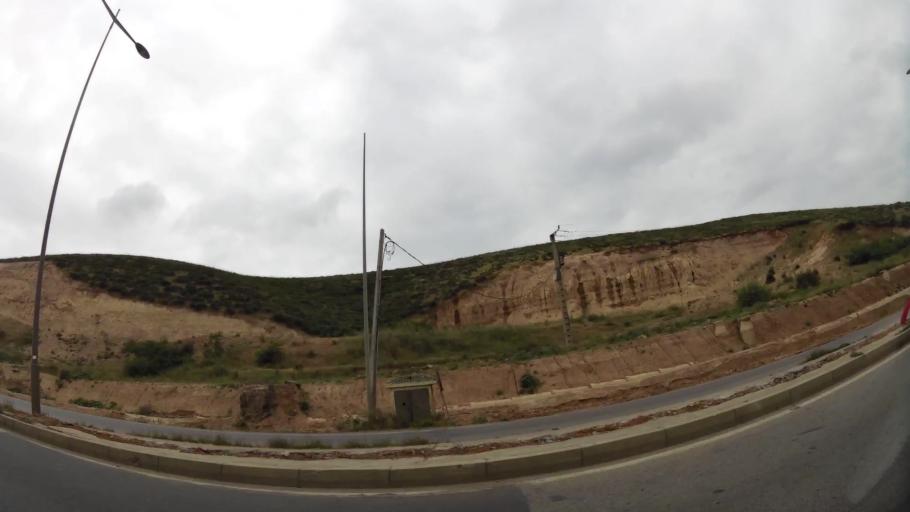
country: MA
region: Rabat-Sale-Zemmour-Zaer
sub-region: Rabat
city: Rabat
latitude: 33.9801
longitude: -6.8044
